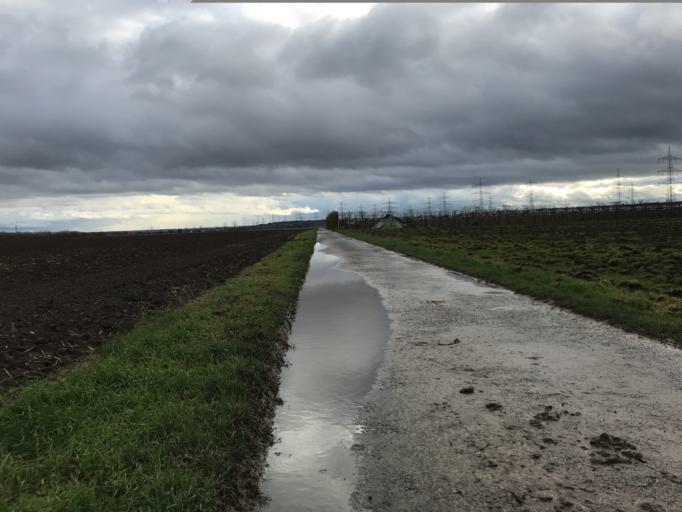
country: DE
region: North Rhine-Westphalia
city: Wesseling
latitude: 50.8251
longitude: 6.9499
